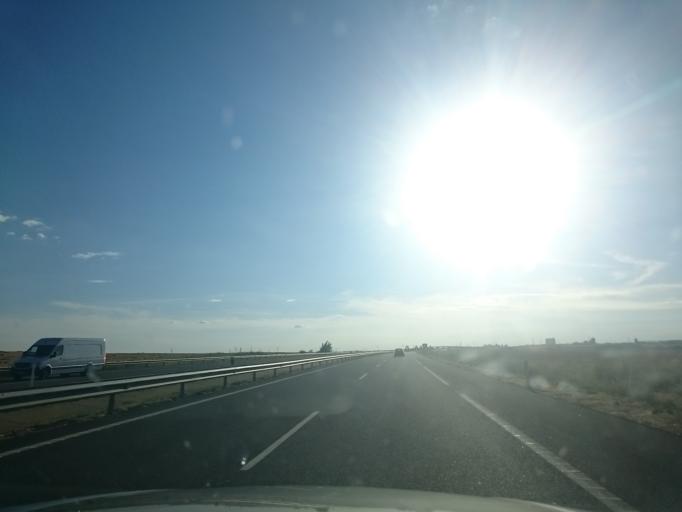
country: ES
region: Castille and Leon
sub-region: Provincia de Palencia
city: Osornillo
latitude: 42.4010
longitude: -4.3356
